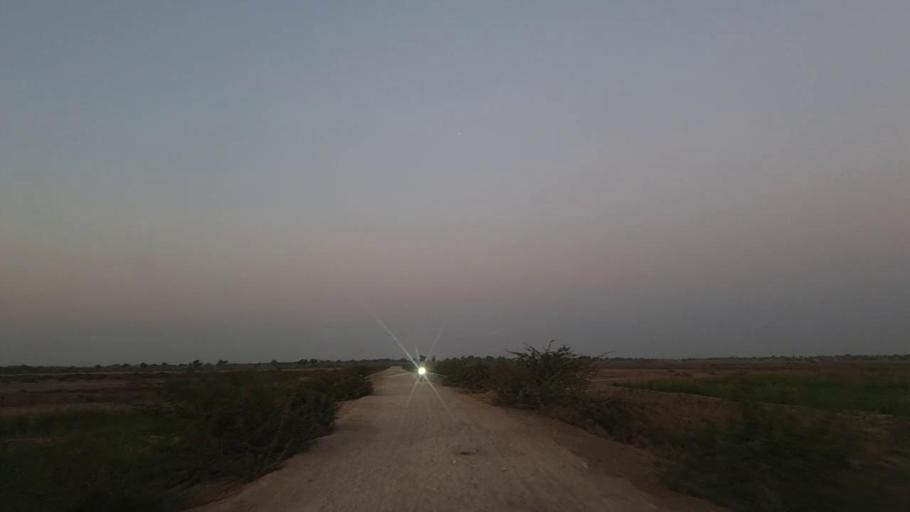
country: PK
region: Sindh
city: Naukot
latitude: 24.8815
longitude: 69.3900
